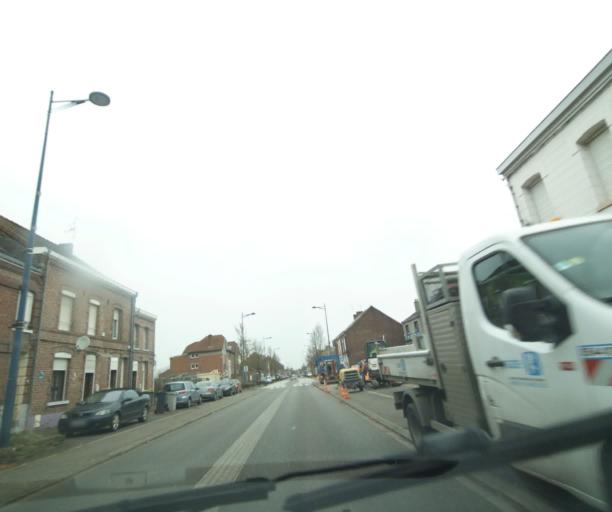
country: FR
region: Nord-Pas-de-Calais
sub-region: Departement du Nord
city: Crespin
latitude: 50.4086
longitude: 3.6642
